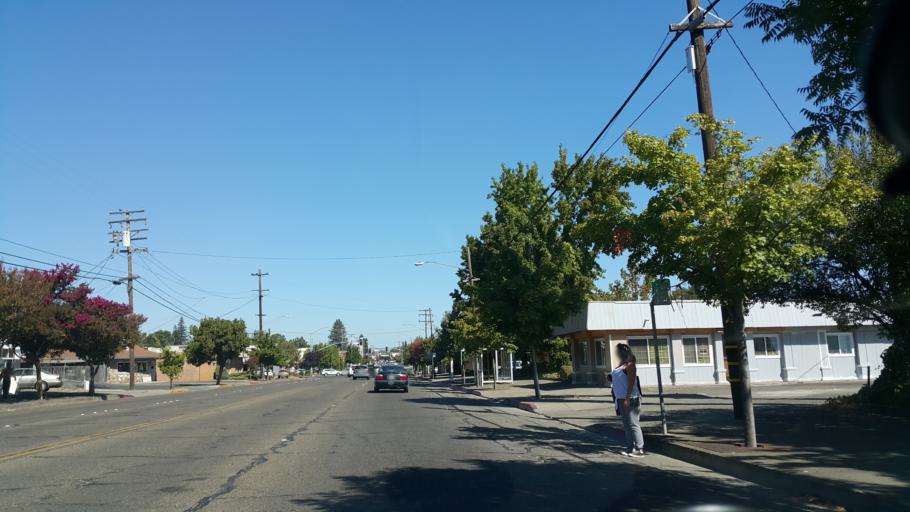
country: US
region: California
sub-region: Mendocino County
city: Ukiah
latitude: 39.1417
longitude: -123.2062
